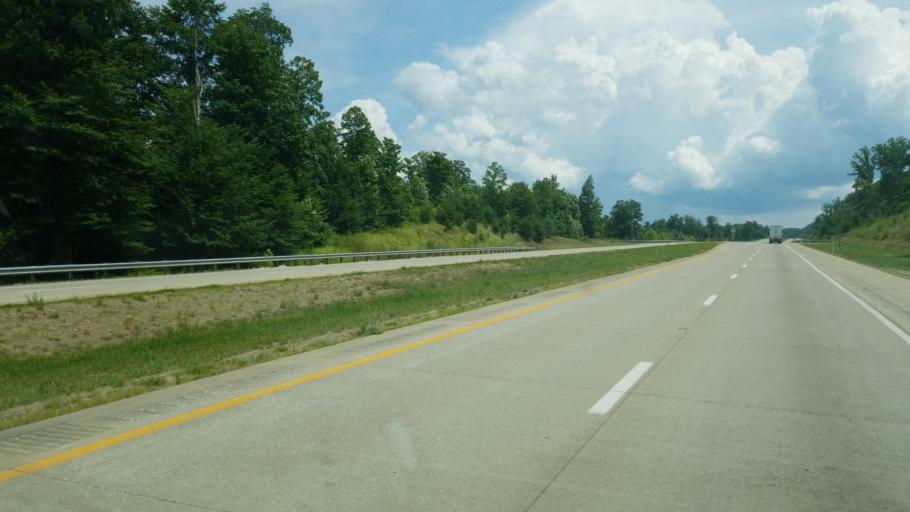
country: US
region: West Virginia
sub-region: Putnam County
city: Eleanor
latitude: 38.5411
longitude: -81.9661
